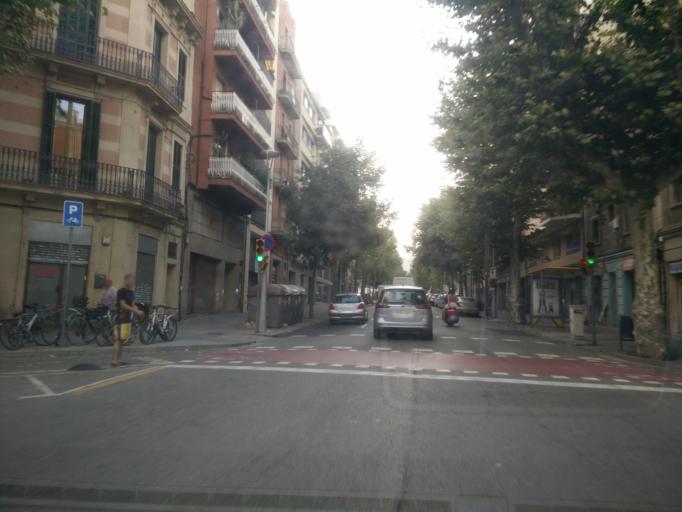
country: ES
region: Catalonia
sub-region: Provincia de Barcelona
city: Sant Marti
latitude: 41.4061
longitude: 2.1856
